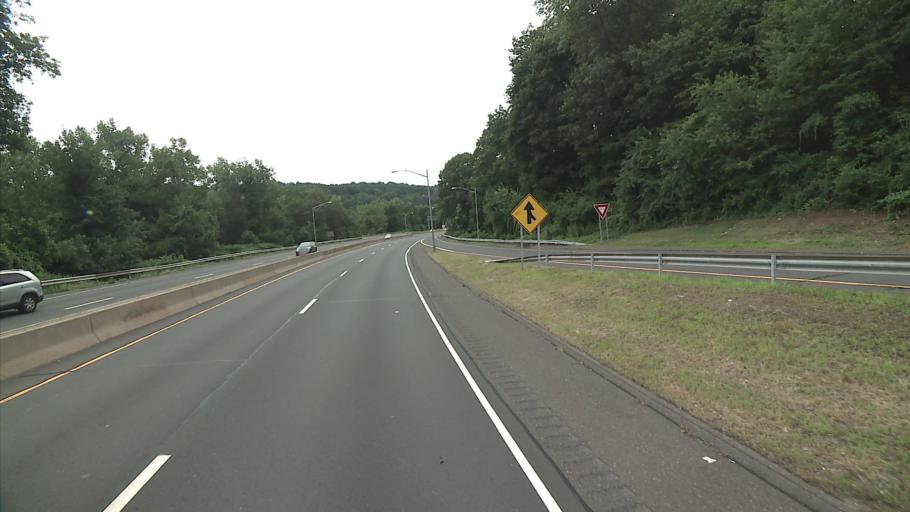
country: US
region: Connecticut
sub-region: New Haven County
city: Derby
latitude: 41.3288
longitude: -73.0872
